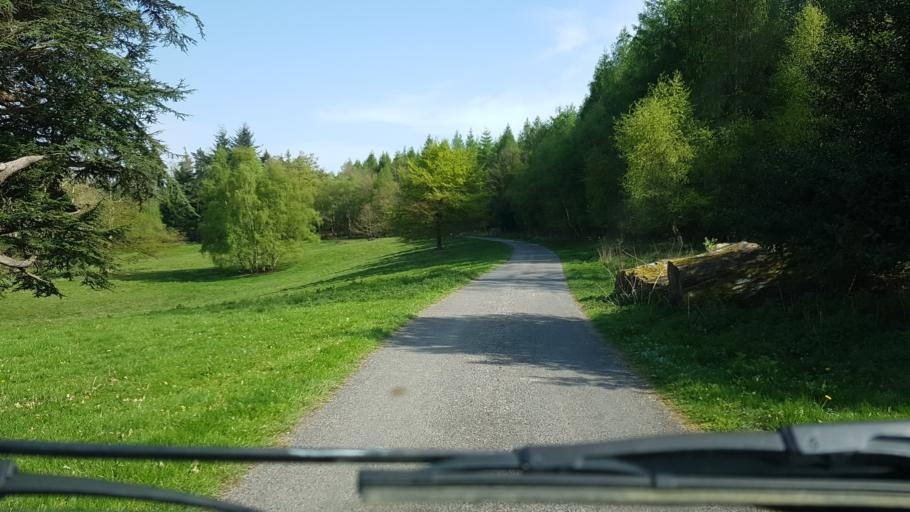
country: GB
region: England
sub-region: Hampshire
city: Highclere
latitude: 51.3378
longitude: -1.3463
